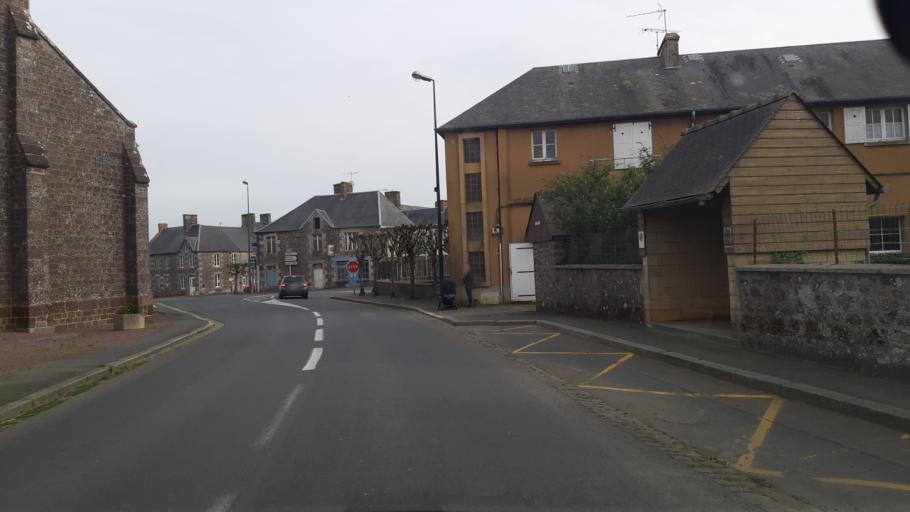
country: FR
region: Lower Normandy
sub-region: Departement de la Manche
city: Gavray
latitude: 48.9406
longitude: -1.3300
